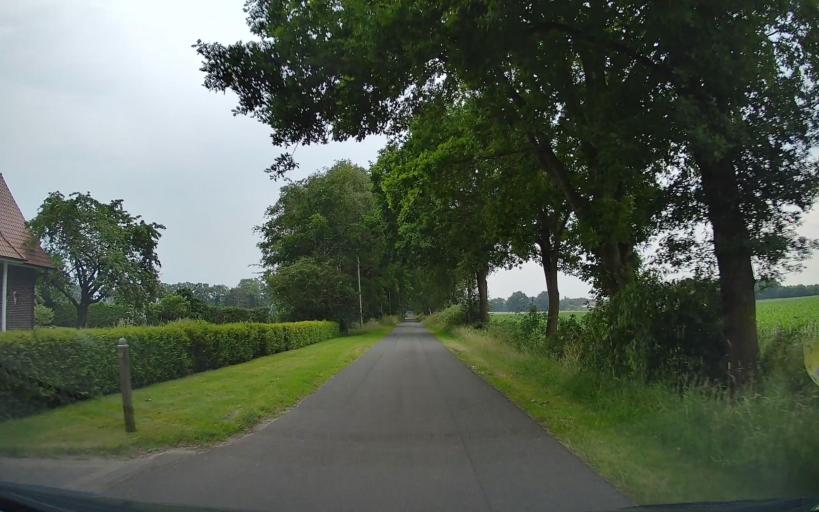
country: DE
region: Lower Saxony
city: Friesoythe
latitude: 53.0544
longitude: 7.8640
